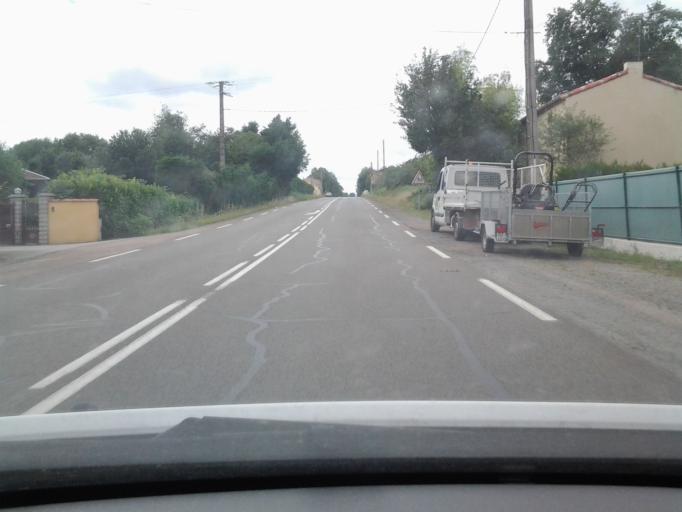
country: FR
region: Pays de la Loire
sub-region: Departement de la Vendee
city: Les Clouzeaux
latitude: 46.6550
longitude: -1.4896
